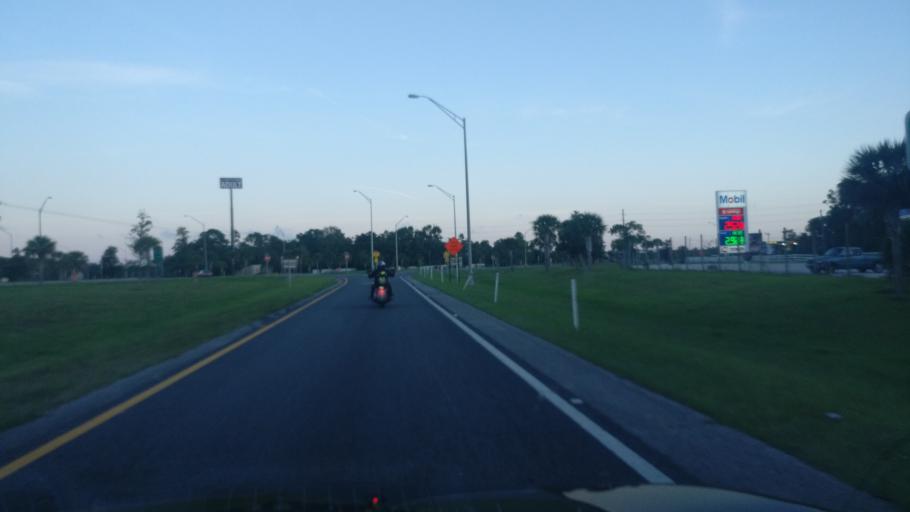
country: US
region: Florida
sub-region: Flagler County
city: Palm Coast
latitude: 29.6621
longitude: -81.2886
